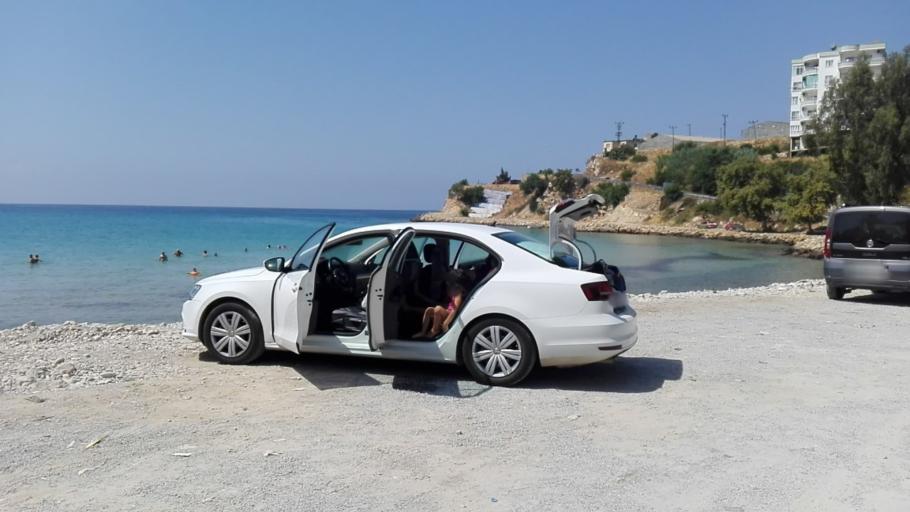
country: TR
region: Mersin
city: Aydincik
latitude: 36.1358
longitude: 33.2960
